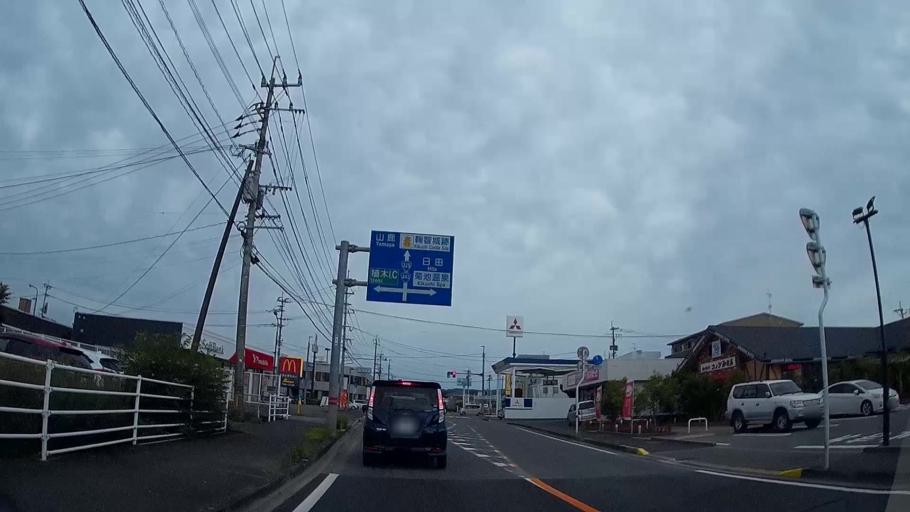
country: JP
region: Kumamoto
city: Kikuchi
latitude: 32.9740
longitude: 130.8087
